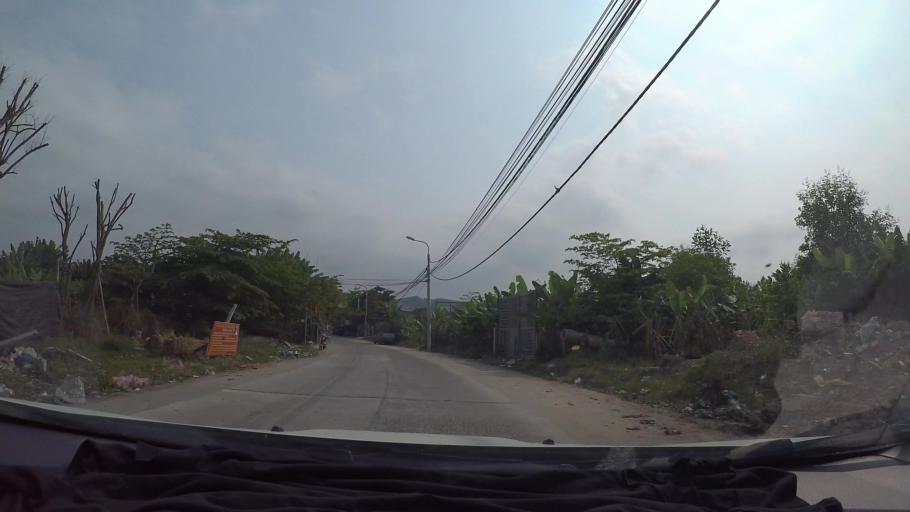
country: VN
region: Da Nang
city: Lien Chieu
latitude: 16.0580
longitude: 108.1567
